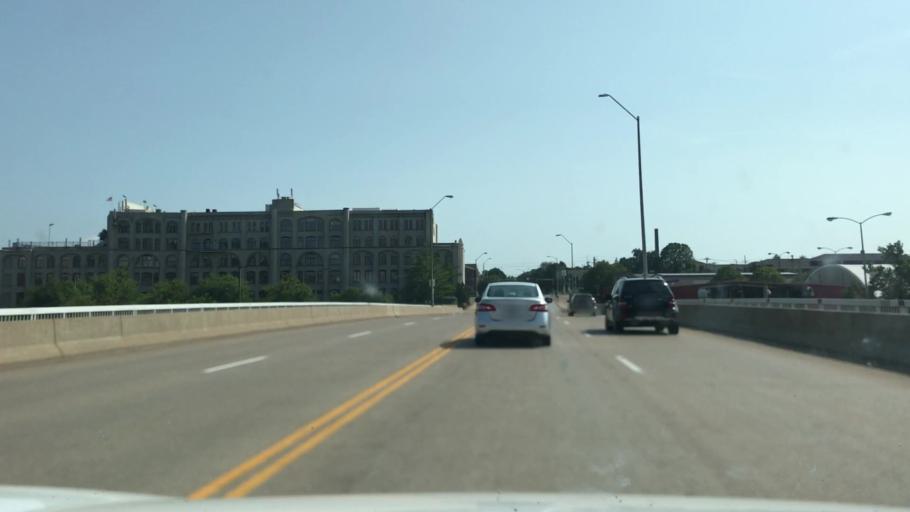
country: US
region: Missouri
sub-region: City of Saint Louis
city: St. Louis
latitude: 38.6218
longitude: -90.2037
